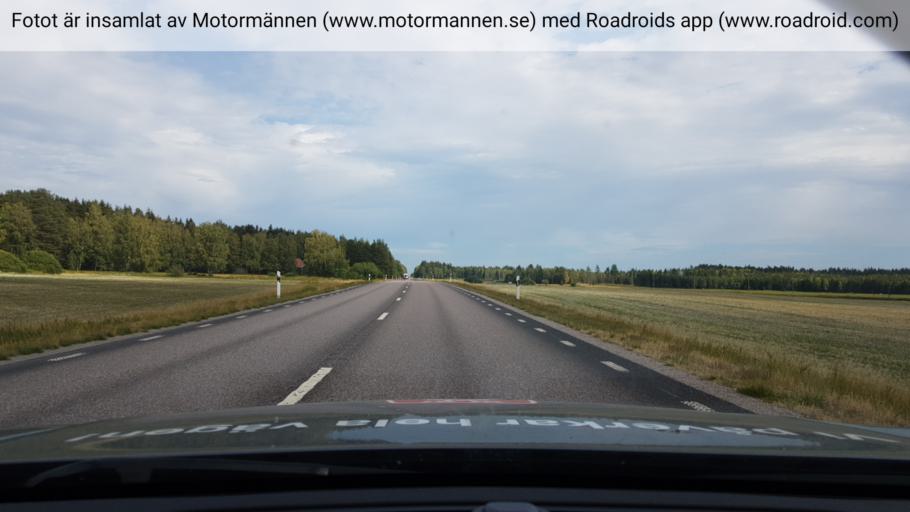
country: SE
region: Uppsala
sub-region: Enkopings Kommun
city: Orsundsbro
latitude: 59.8720
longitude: 17.3015
